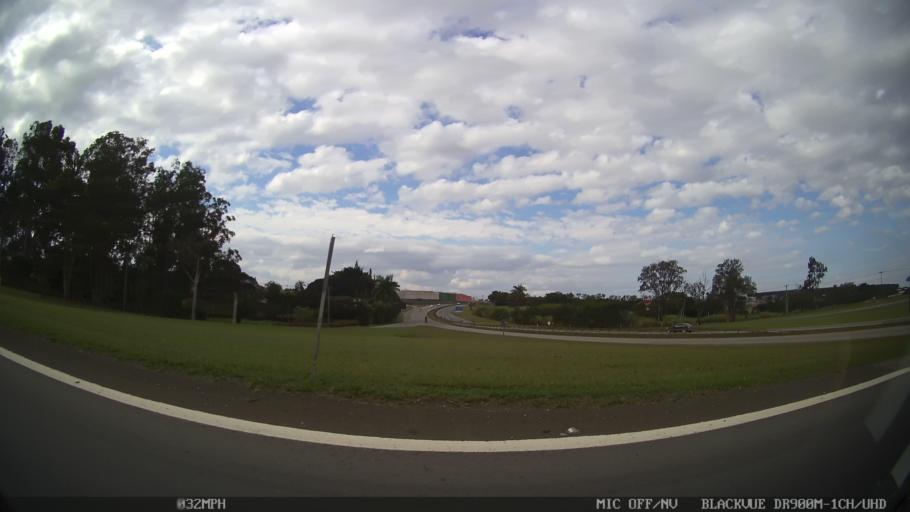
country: BR
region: Sao Paulo
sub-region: Limeira
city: Limeira
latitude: -22.5441
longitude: -47.3754
